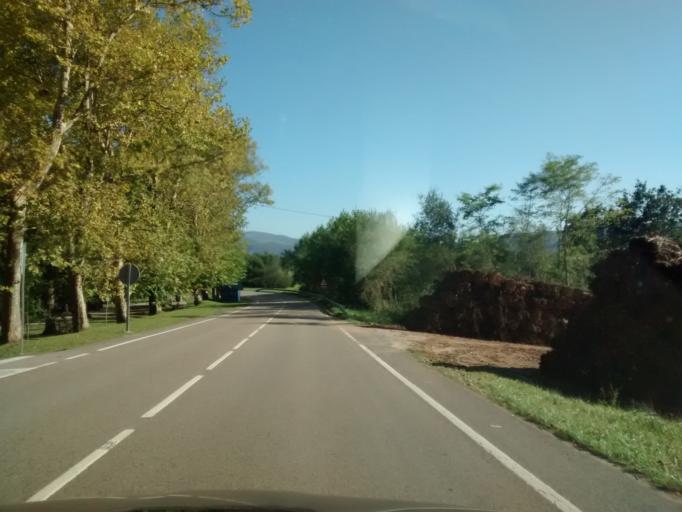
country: ES
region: Cantabria
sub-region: Provincia de Cantabria
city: Cabezon de la Sal
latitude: 43.3296
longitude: -4.2636
